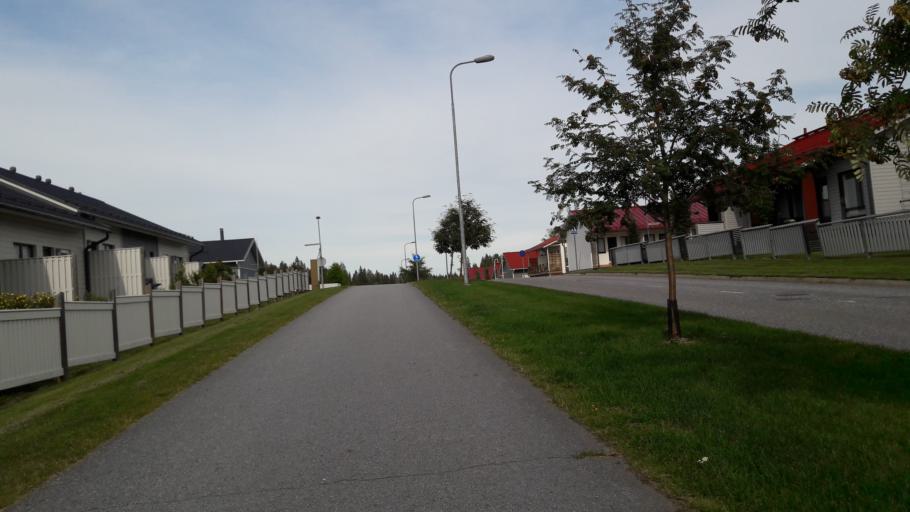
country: FI
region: North Karelia
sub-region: Joensuu
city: Joensuu
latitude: 62.5711
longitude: 29.8218
